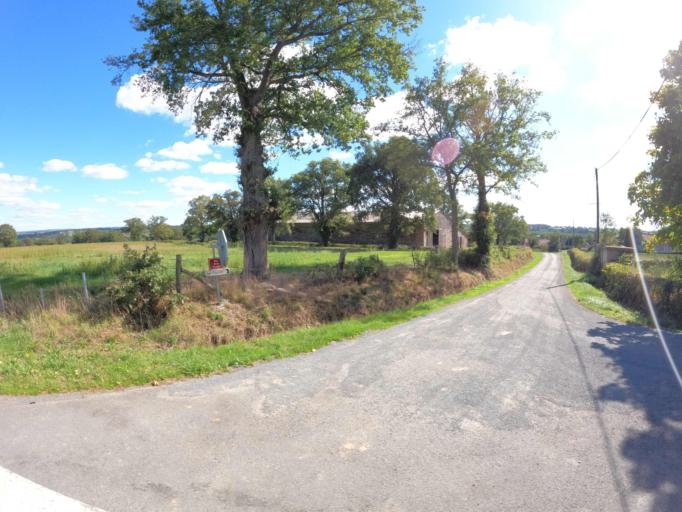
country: FR
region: Auvergne
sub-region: Departement de l'Allier
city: Doyet
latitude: 46.3846
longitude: 2.7896
